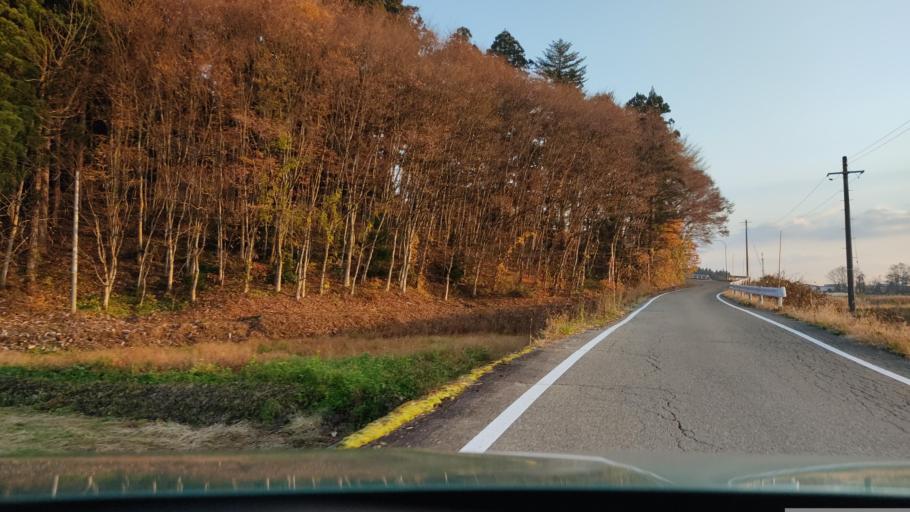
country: JP
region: Akita
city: Omagari
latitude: 39.4215
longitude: 140.5853
